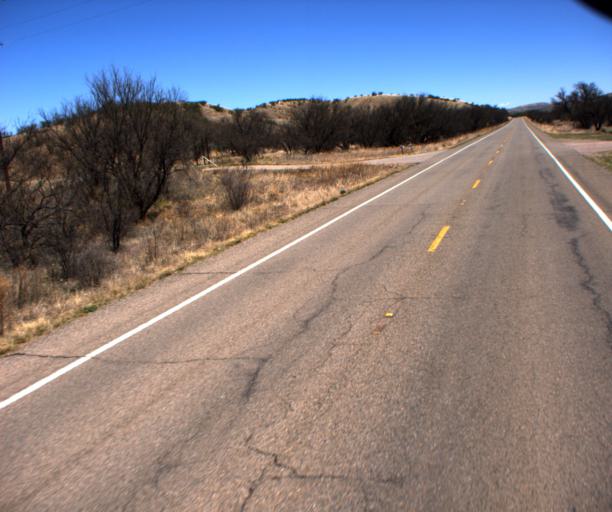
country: US
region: Arizona
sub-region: Santa Cruz County
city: Rio Rico
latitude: 31.5611
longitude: -110.7336
